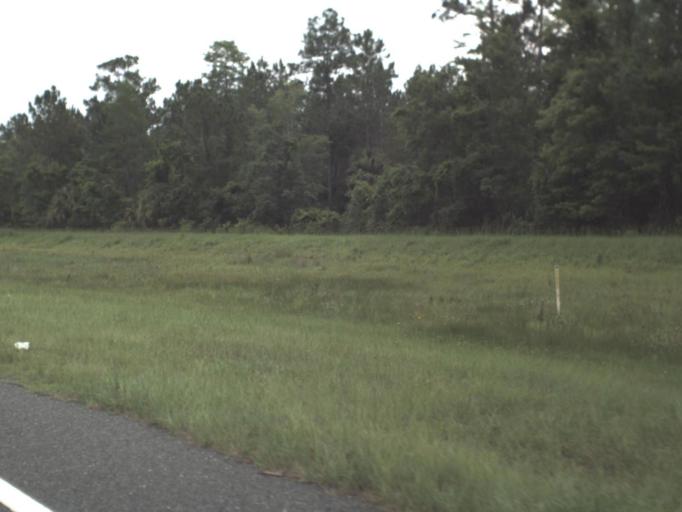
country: US
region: Florida
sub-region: Levy County
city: Chiefland
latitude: 29.3510
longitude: -82.7828
